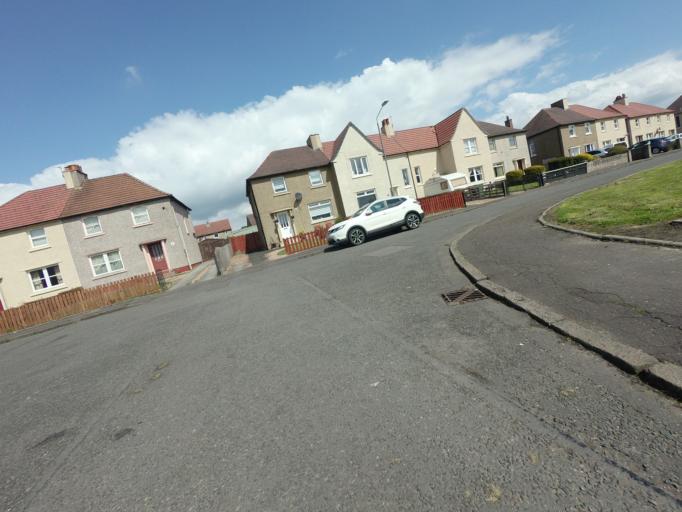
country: GB
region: Scotland
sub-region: Falkirk
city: Falkirk
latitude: 56.0279
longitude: -3.7864
